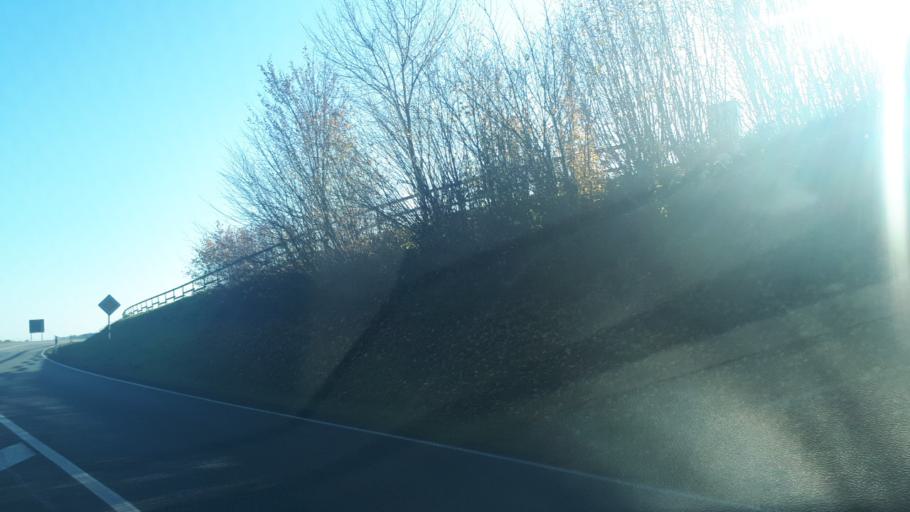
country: DE
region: Rheinland-Pfalz
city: Buchel
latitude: 50.1885
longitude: 7.0751
